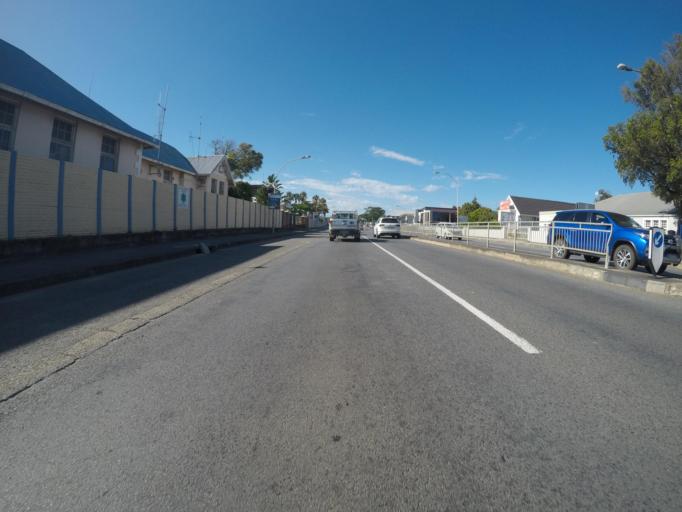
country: ZA
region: Eastern Cape
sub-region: Buffalo City Metropolitan Municipality
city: East London
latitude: -32.9763
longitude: 27.8993
